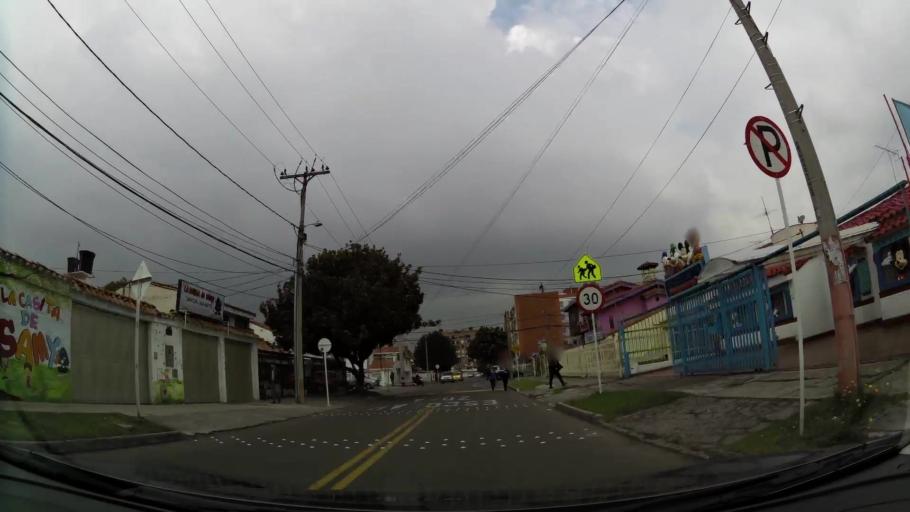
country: CO
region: Bogota D.C.
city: Barrio San Luis
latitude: 4.7239
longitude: -74.0479
